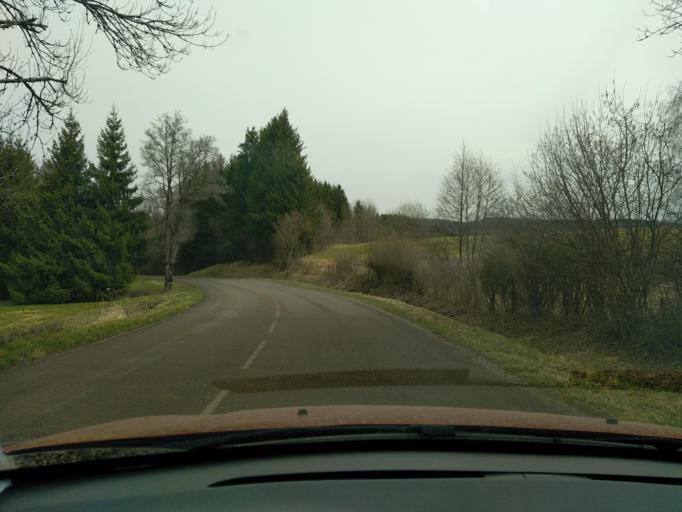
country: FR
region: Franche-Comte
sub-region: Departement du Jura
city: Clairvaux-les-Lacs
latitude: 46.6054
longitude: 5.7282
